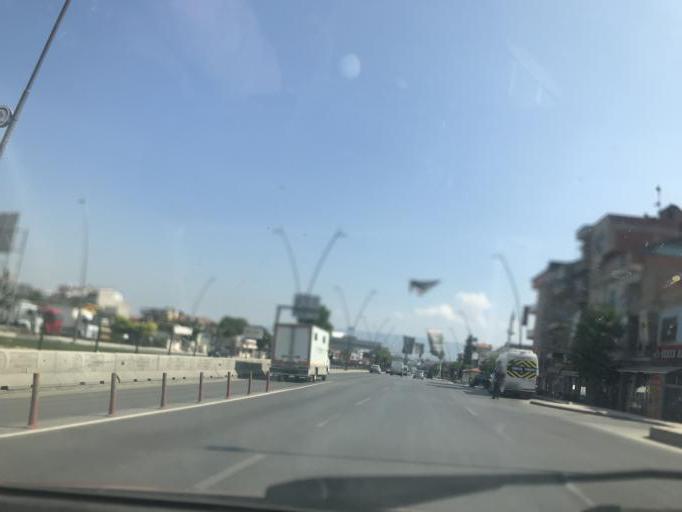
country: TR
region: Denizli
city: Denizli
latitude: 37.7842
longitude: 29.0980
